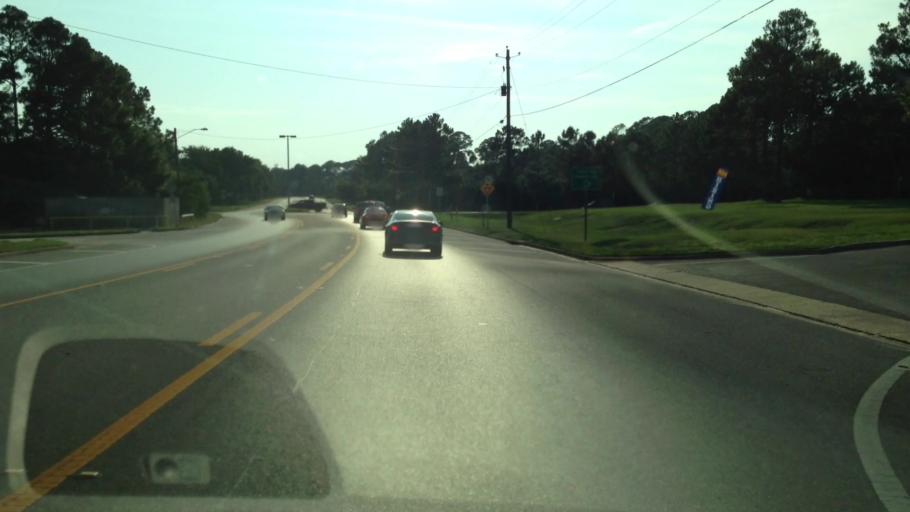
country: US
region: Florida
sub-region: Okaloosa County
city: Mary Esther
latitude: 30.4140
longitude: -86.6667
